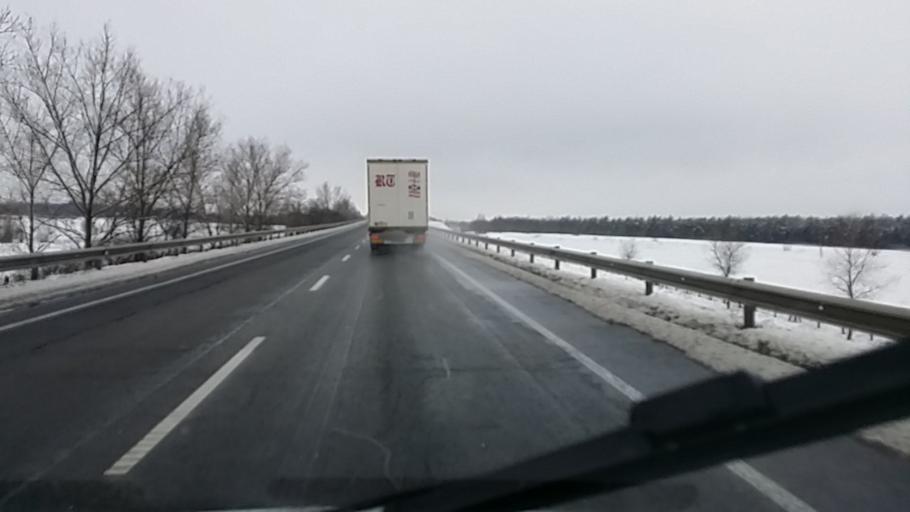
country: HU
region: Gyor-Moson-Sopron
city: Rajka
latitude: 47.9290
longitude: 17.1717
